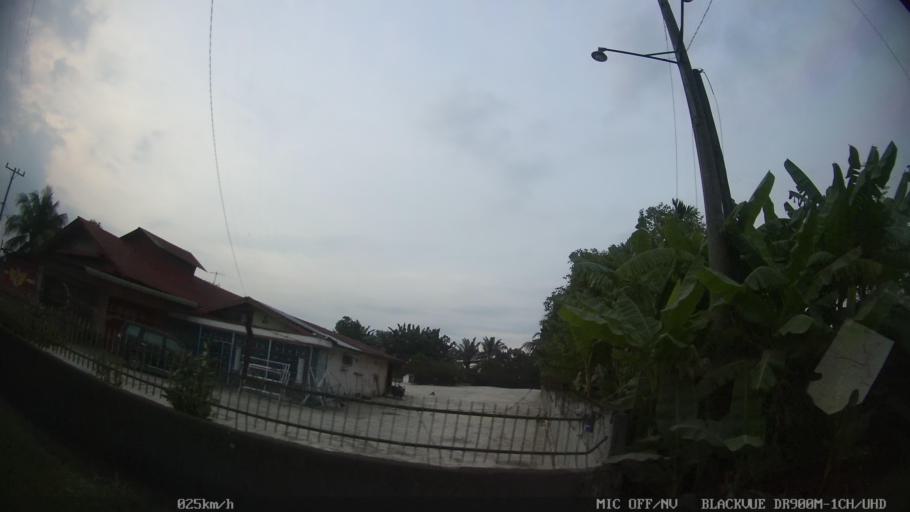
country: ID
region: North Sumatra
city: Sunggal
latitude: 3.5849
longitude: 98.5926
